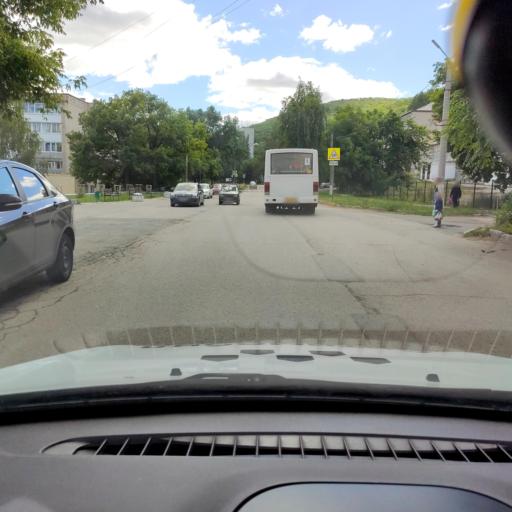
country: RU
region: Samara
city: Zhigulevsk
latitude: 53.4067
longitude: 49.4066
